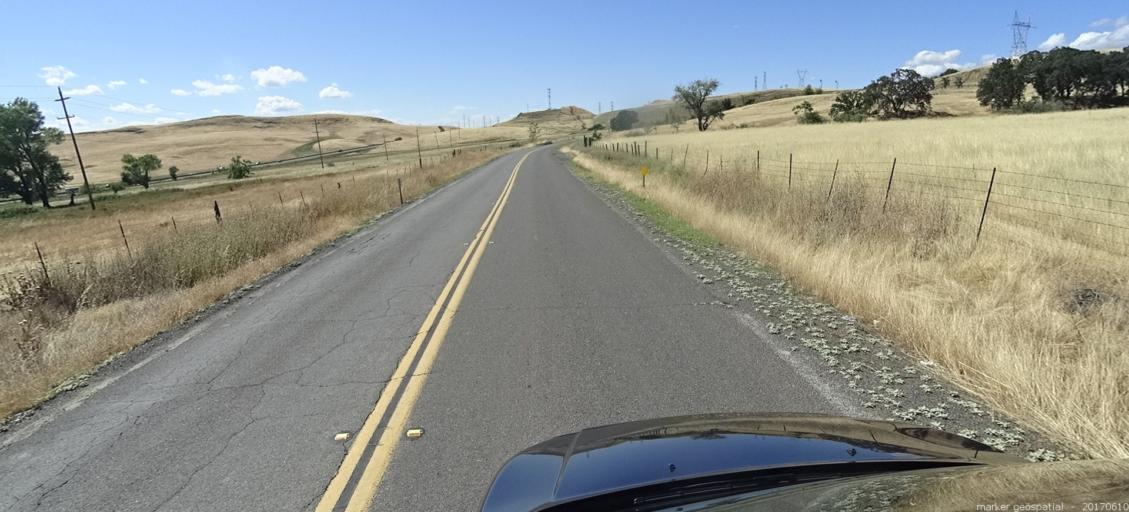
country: US
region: California
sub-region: Butte County
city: Thermalito
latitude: 39.5387
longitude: -121.5822
